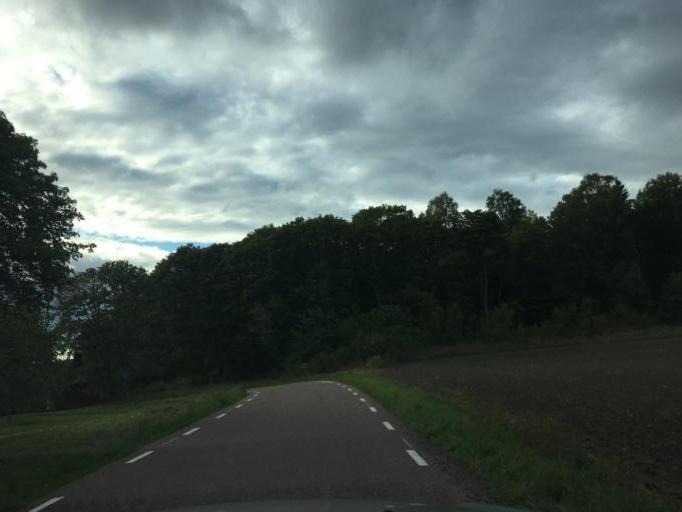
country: SE
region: Vaestmanland
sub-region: Vasteras
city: Tillberga
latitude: 59.5831
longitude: 16.6922
